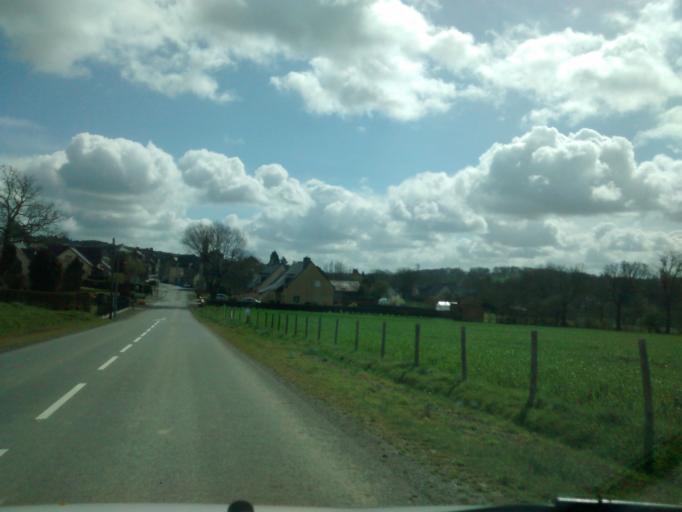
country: FR
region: Brittany
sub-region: Departement d'Ille-et-Vilaine
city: Livre-sur-Changeon
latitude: 48.1933
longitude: -1.3744
